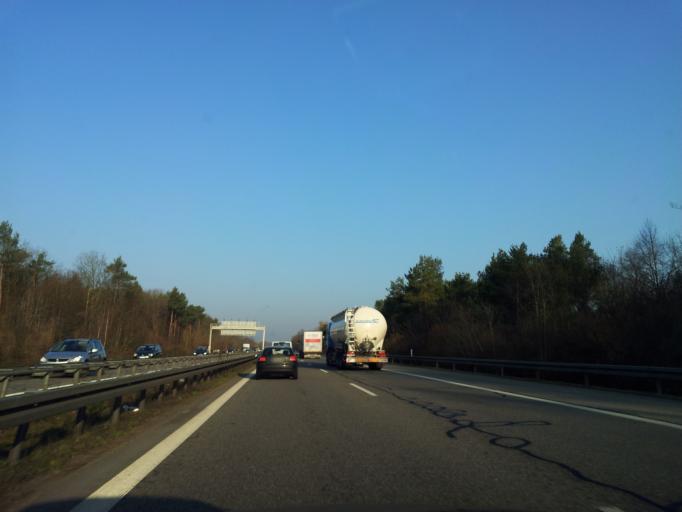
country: DE
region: Baden-Wuerttemberg
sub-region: Freiburg Region
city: Efringen-Kirchen
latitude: 47.6436
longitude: 7.5544
